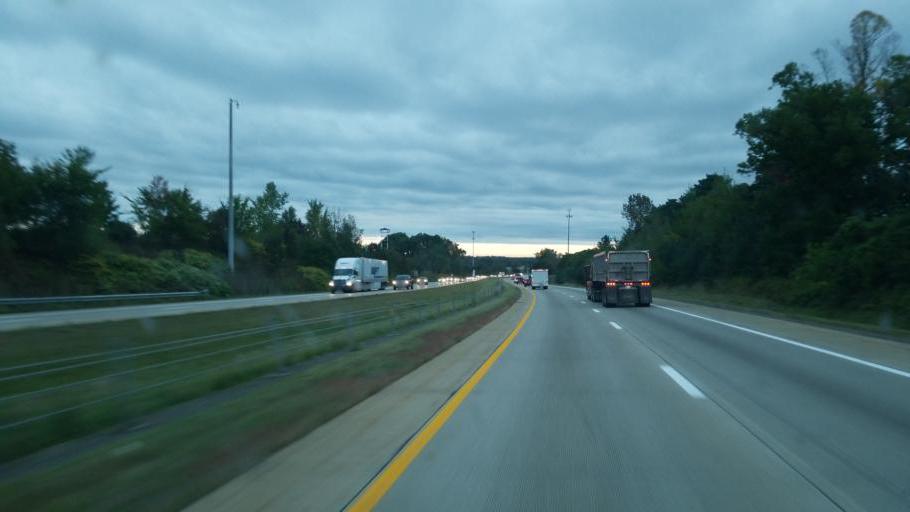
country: US
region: Ohio
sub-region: Portage County
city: Brimfield
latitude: 41.0909
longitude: -81.3847
